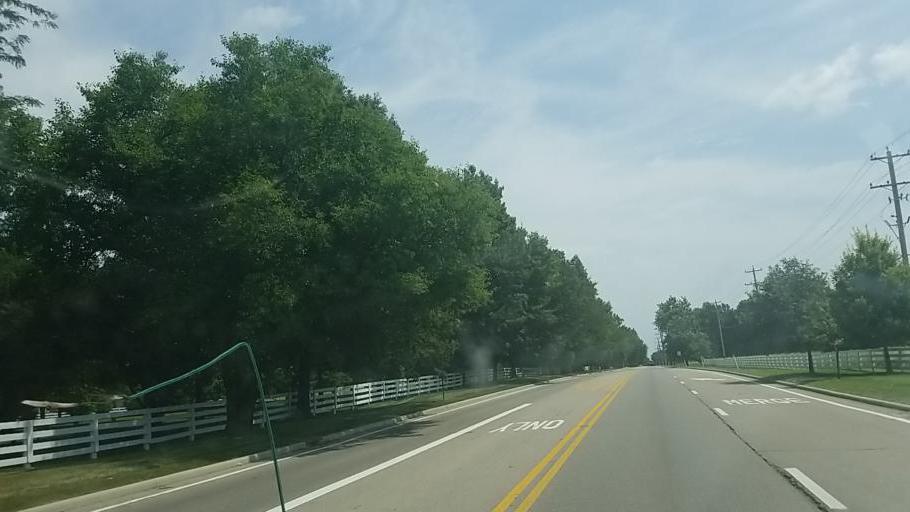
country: US
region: Ohio
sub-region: Franklin County
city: New Albany
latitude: 40.0543
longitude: -82.8392
